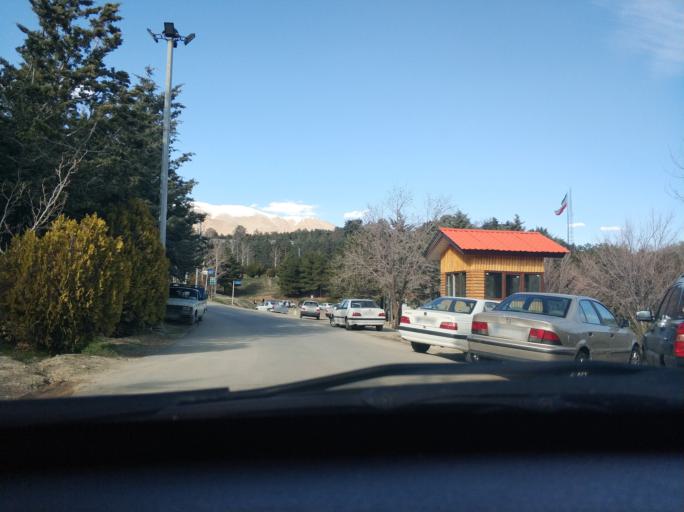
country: IR
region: Tehran
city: Tajrish
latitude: 35.8038
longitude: 51.5687
